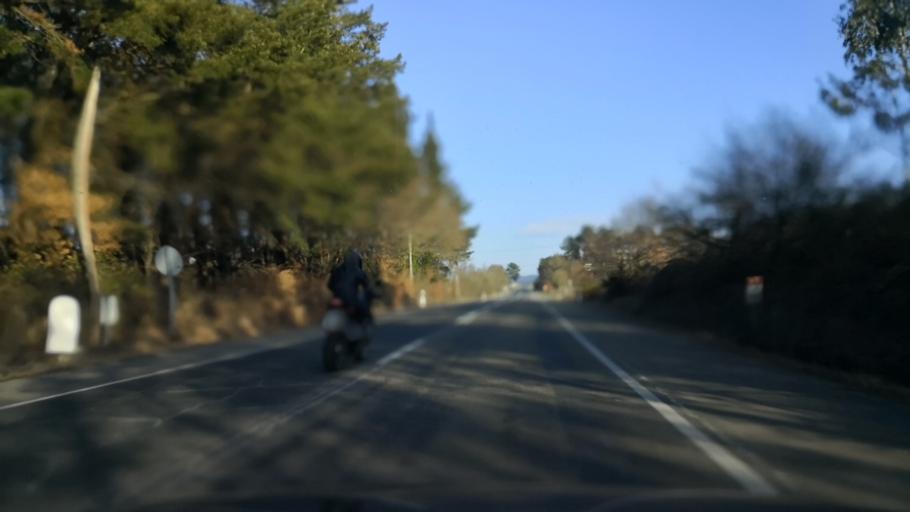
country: ES
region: Galicia
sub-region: Provincia de Lugo
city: Corgo
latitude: 42.9377
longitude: -7.4136
